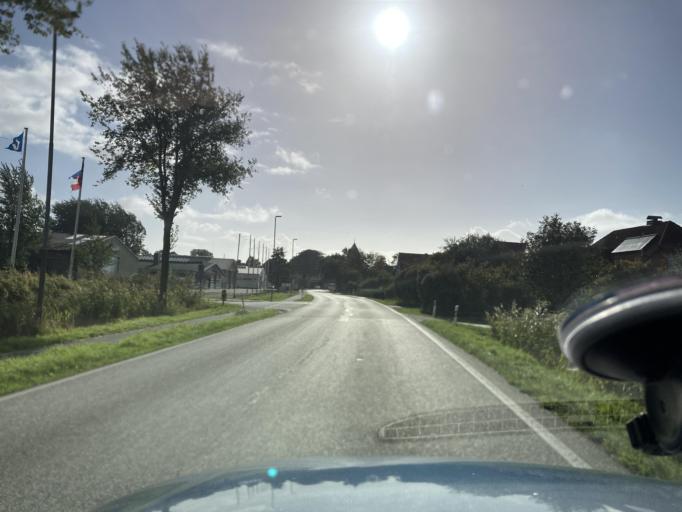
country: DE
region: Schleswig-Holstein
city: Wohrden
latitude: 54.1682
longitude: 9.0012
